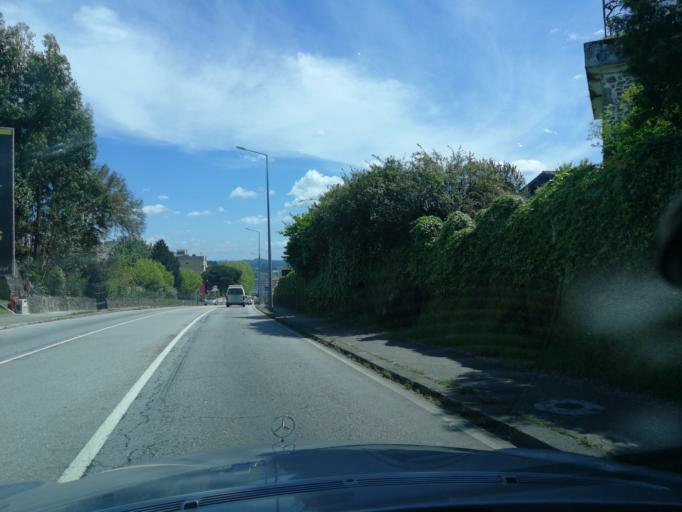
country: PT
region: Braga
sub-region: Vila Nova de Famalicao
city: Vila Nova de Famalicao
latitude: 41.4159
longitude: -8.5278
